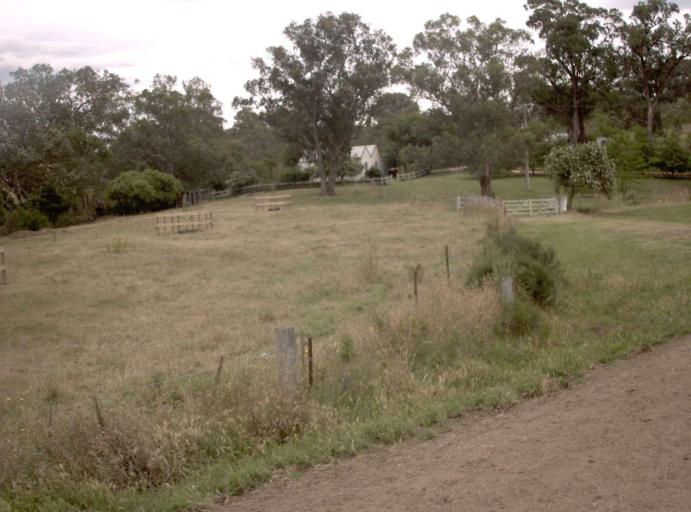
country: AU
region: Victoria
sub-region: East Gippsland
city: Bairnsdale
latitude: -37.7667
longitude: 147.3214
